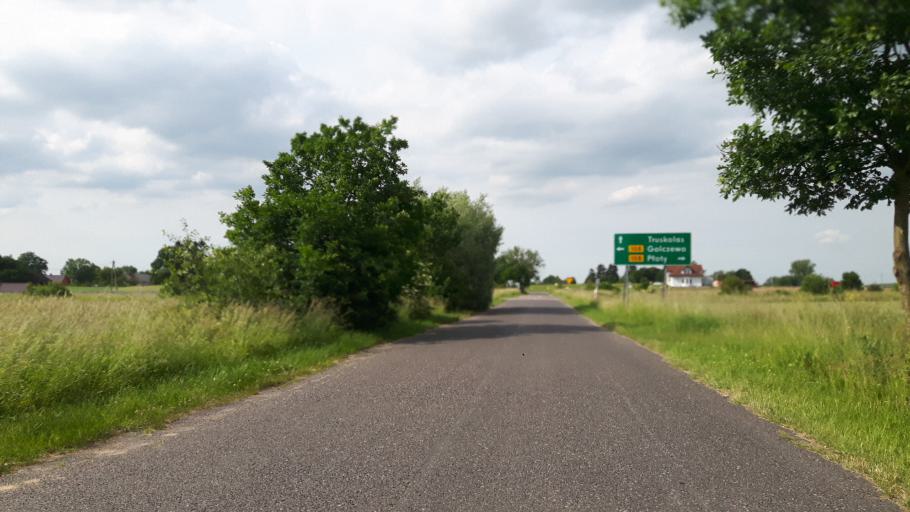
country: PL
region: West Pomeranian Voivodeship
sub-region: Powiat gryficki
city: Gryfice
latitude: 53.8121
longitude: 15.1291
